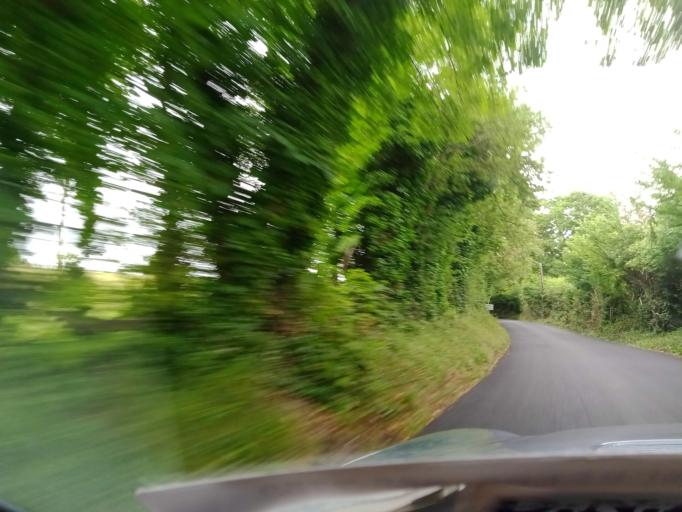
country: IE
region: Leinster
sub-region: Kilkenny
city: Thomastown
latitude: 52.5460
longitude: -7.2259
